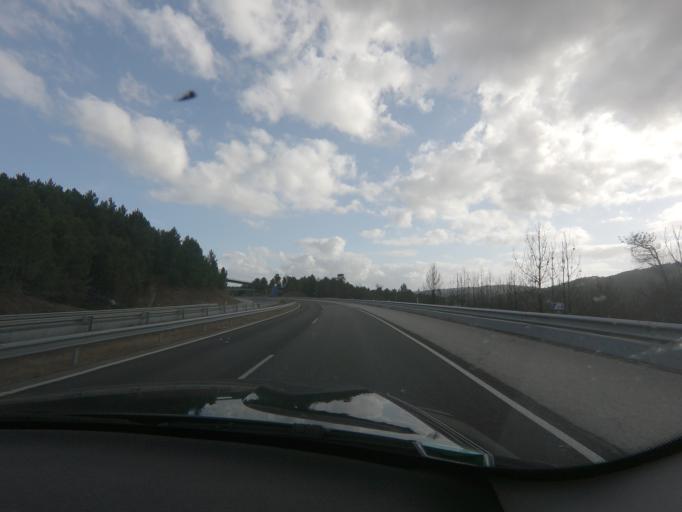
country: PT
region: Viseu
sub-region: Castro Daire
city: Castro Daire
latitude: 40.8687
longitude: -7.9271
